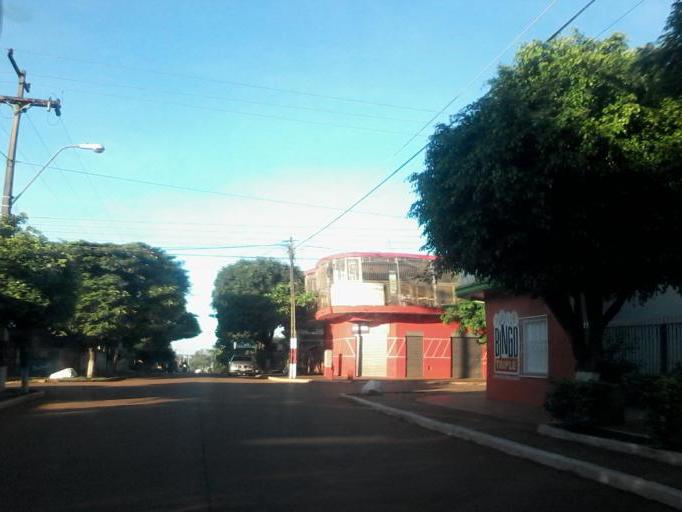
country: PY
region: Alto Parana
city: Ciudad del Este
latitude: -25.4367
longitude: -54.6420
